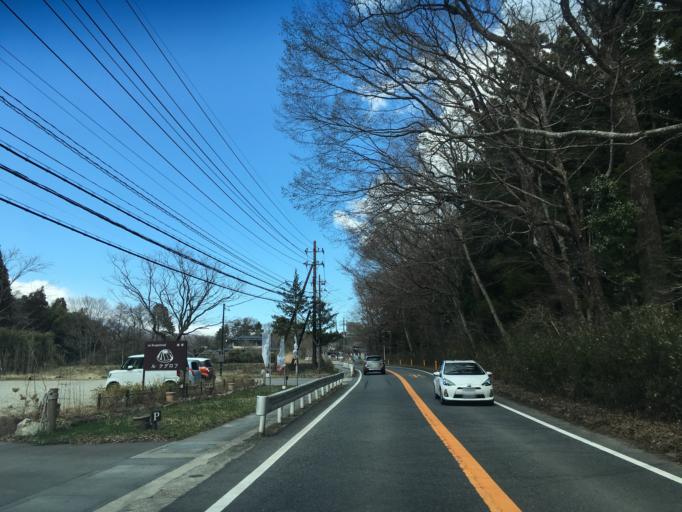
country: JP
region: Tochigi
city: Kuroiso
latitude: 37.0467
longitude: 140.0135
